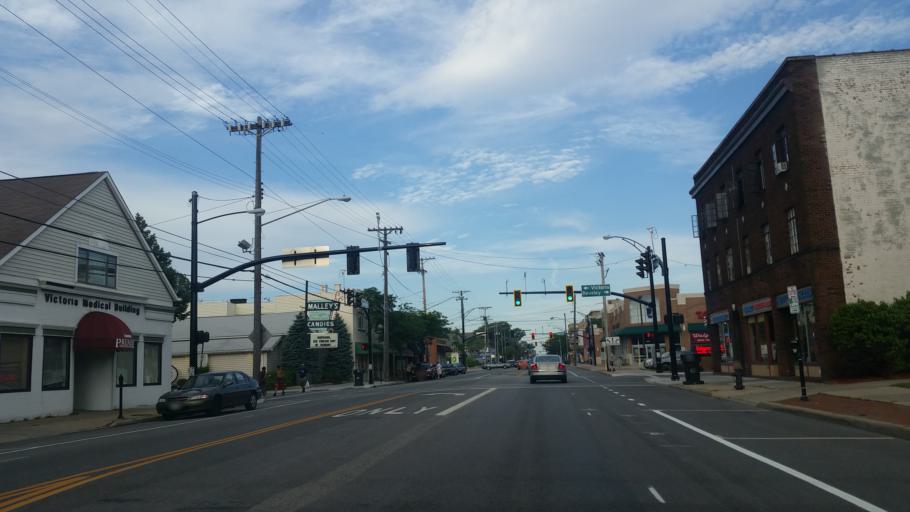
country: US
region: Ohio
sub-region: Cuyahoga County
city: Lakewood
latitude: 41.4772
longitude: -81.8020
